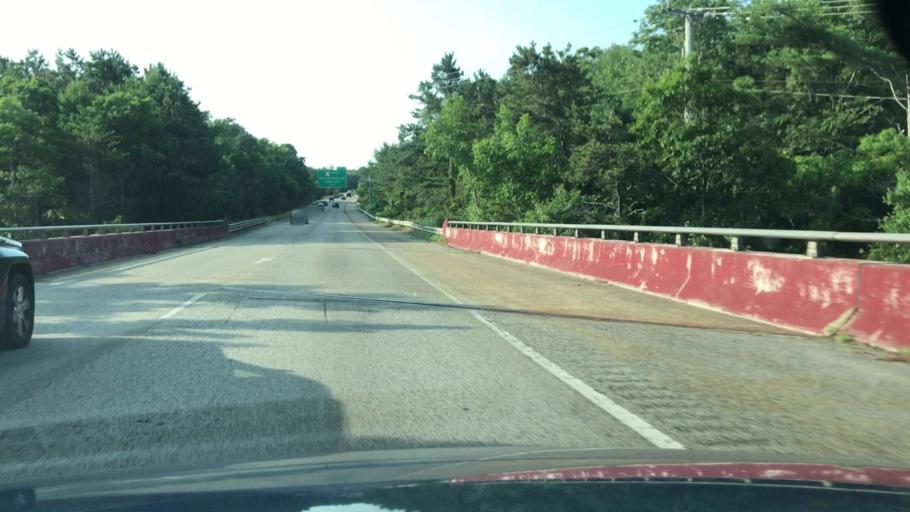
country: US
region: Massachusetts
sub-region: Barnstable County
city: Sagamore
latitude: 41.8301
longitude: -70.5628
